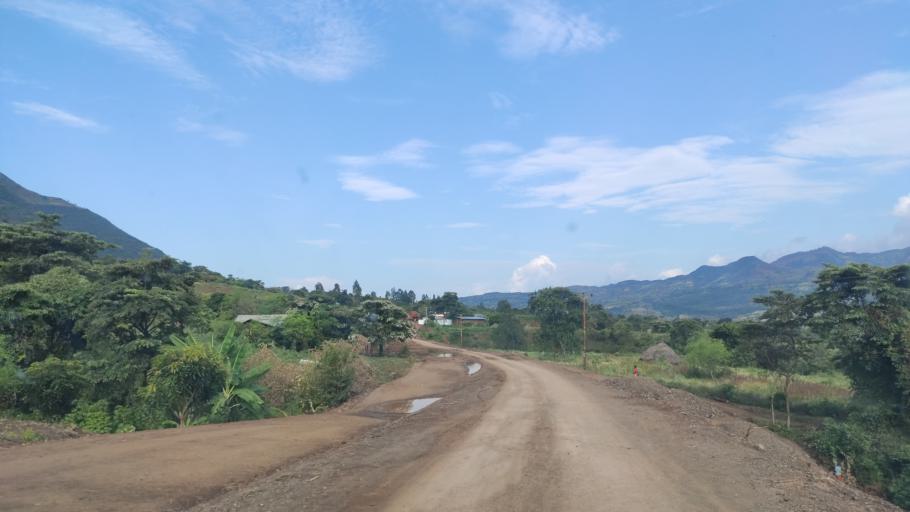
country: ET
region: Southern Nations, Nationalities, and People's Region
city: Arba Minch'
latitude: 6.4245
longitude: 37.3672
